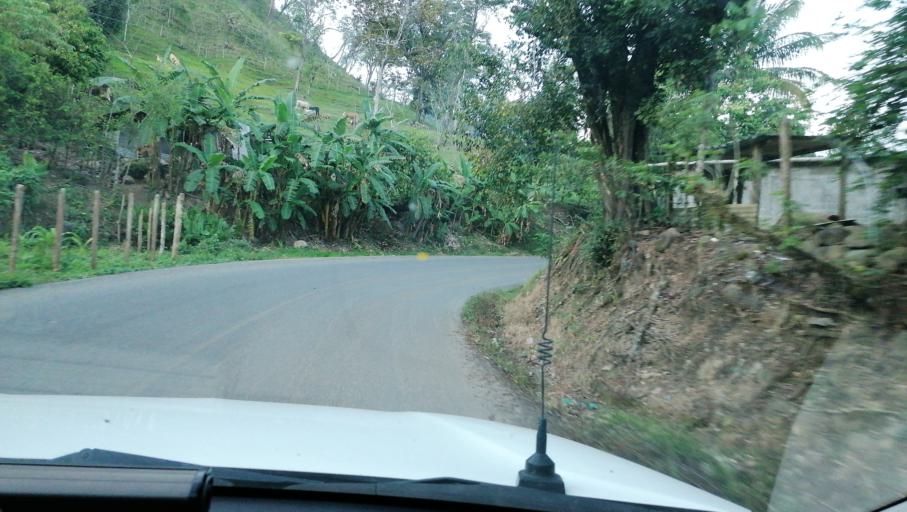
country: MX
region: Chiapas
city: Ostuacan
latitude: 17.4187
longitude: -93.3410
